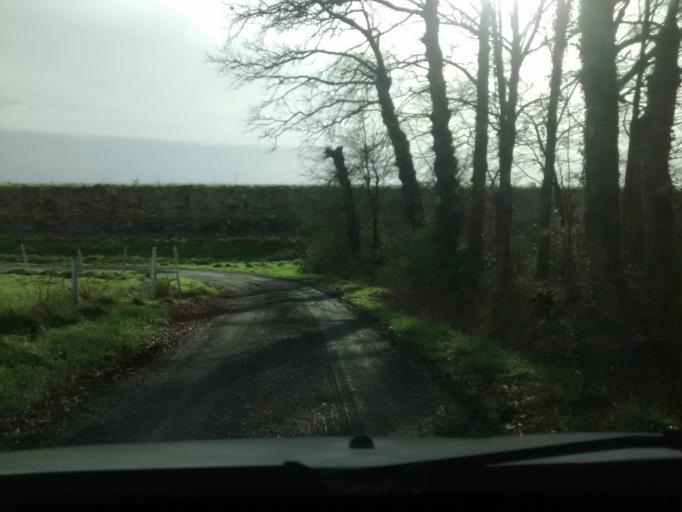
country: FR
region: Brittany
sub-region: Departement d'Ille-et-Vilaine
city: Vezin-le-Coquet
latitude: 48.1273
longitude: -1.7287
